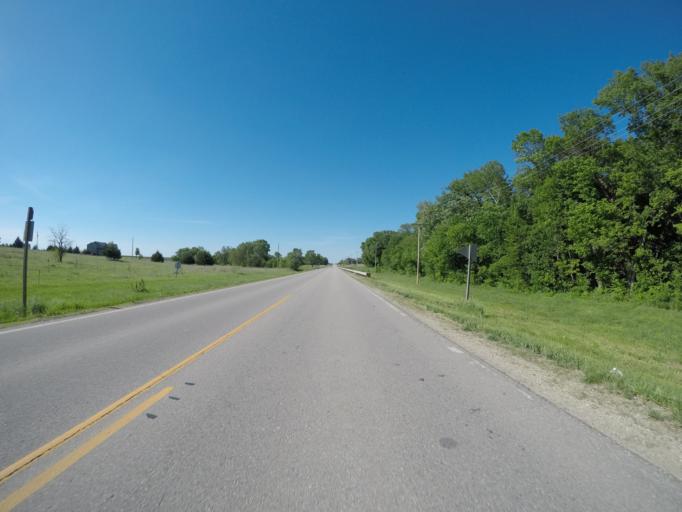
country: US
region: Kansas
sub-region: Riley County
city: Fort Riley North
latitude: 39.3067
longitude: -96.8308
